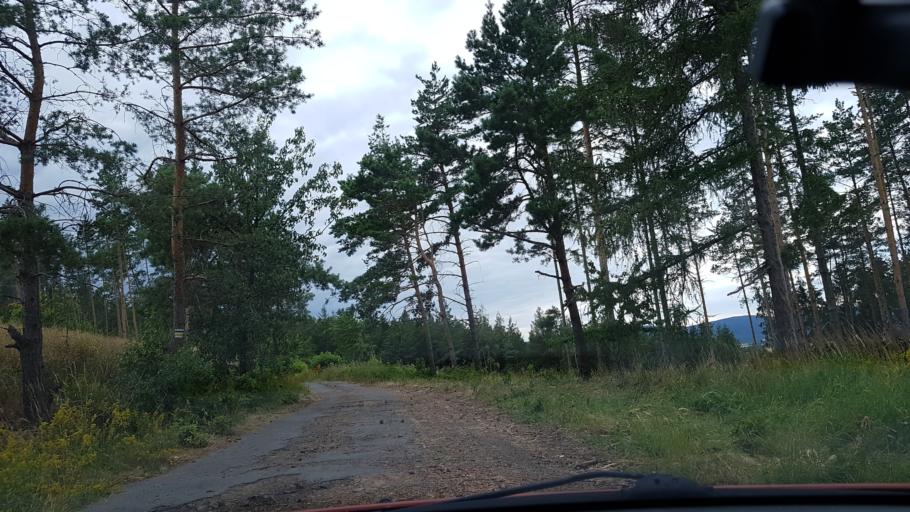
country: PL
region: Lower Silesian Voivodeship
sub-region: Powiat zabkowicki
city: Stoszowice
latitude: 50.5625
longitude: 16.7545
